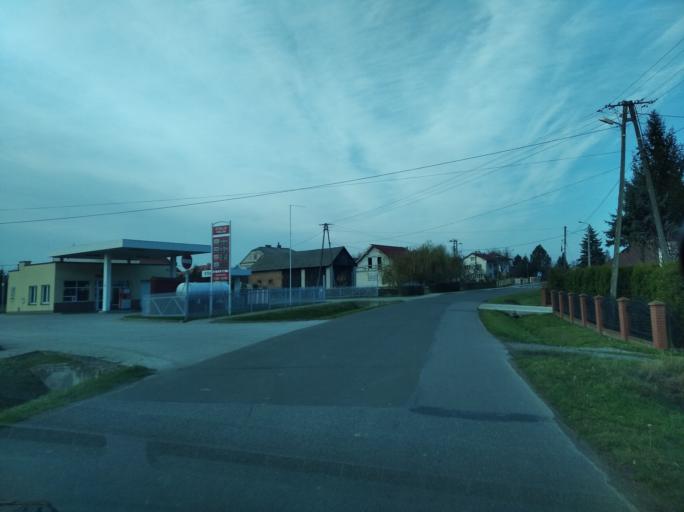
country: PL
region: Subcarpathian Voivodeship
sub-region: Powiat ropczycko-sedziszowski
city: Iwierzyce
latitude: 50.0103
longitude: 21.7546
